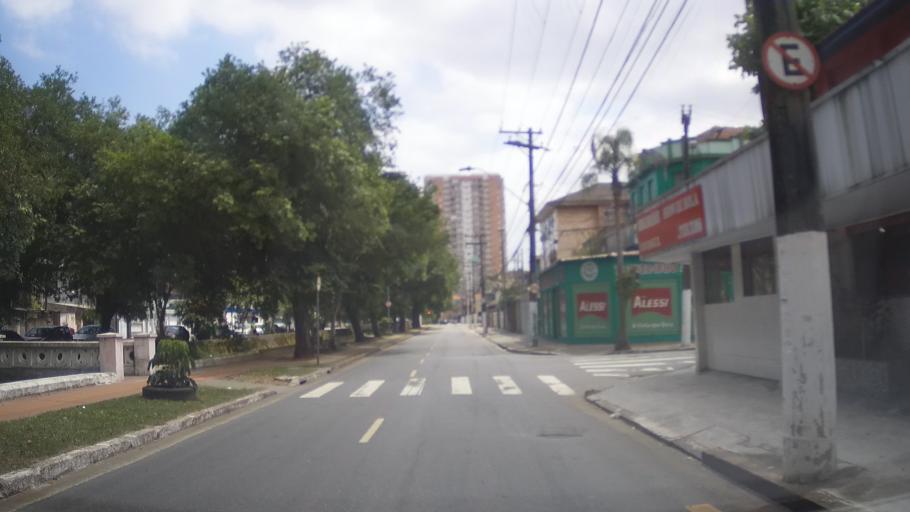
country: BR
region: Sao Paulo
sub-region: Santos
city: Santos
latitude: -23.9603
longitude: -46.3122
